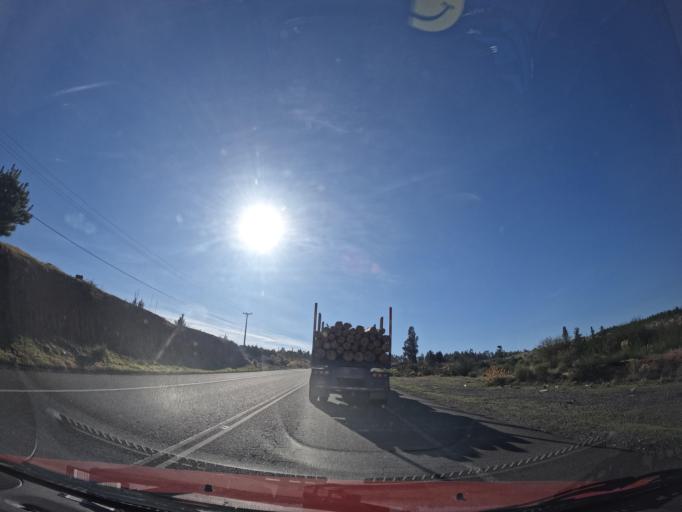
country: CL
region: Maule
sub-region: Provincia de Cauquenes
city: Cauquenes
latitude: -35.9364
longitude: -72.1958
